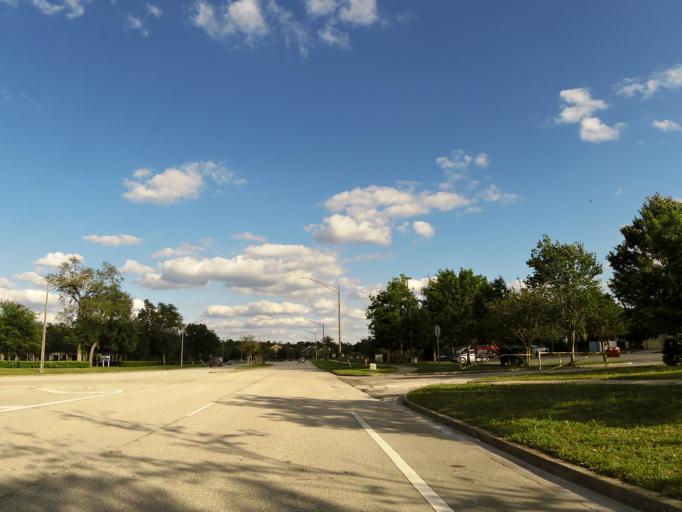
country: US
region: Florida
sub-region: Duval County
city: Jacksonville
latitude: 30.2558
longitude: -81.5801
